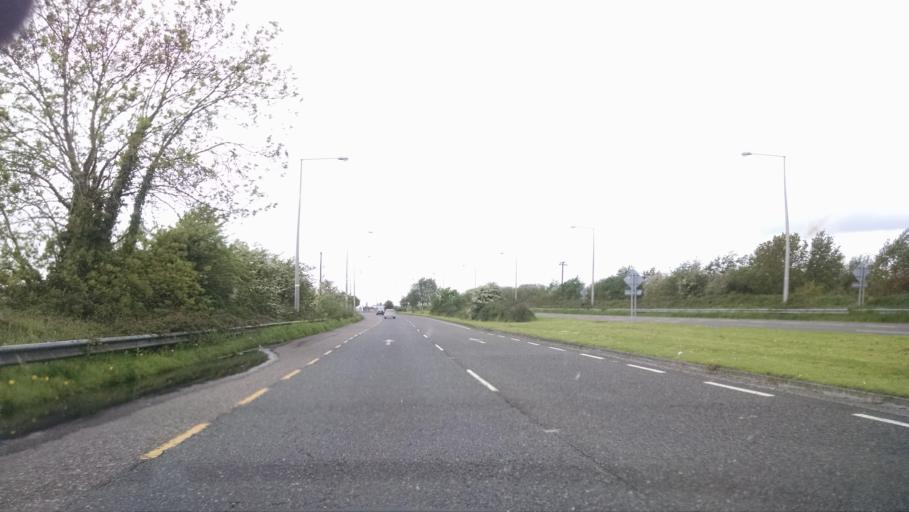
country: IE
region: Munster
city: Moyross
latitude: 52.6771
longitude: -8.6850
